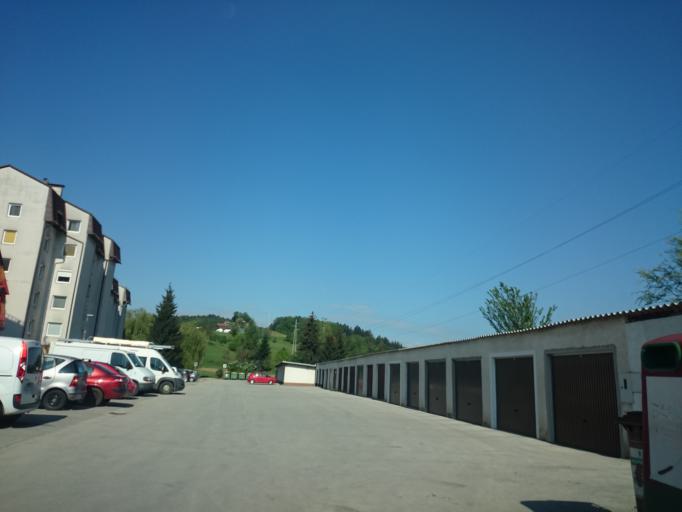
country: SI
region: Sentjur pri Celju
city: Sentjur
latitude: 46.2259
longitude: 15.3946
